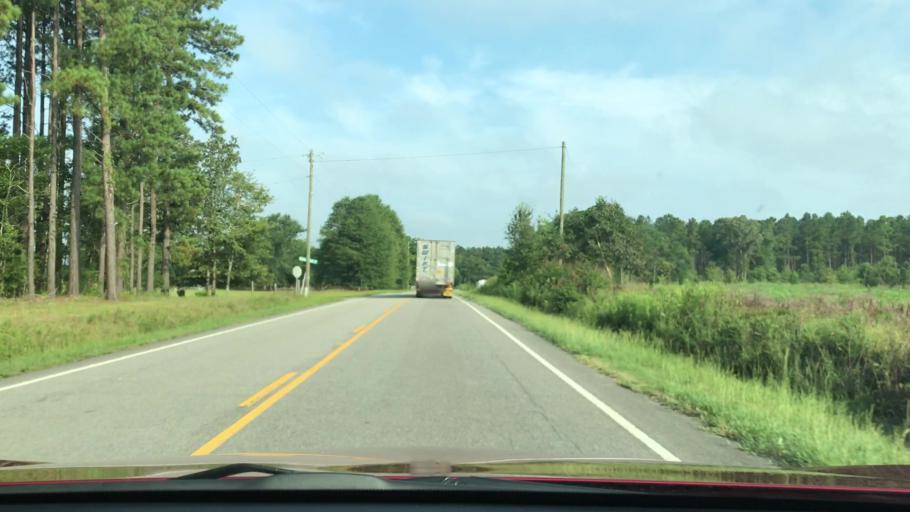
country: US
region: South Carolina
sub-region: Barnwell County
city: Williston
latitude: 33.6133
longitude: -81.2814
